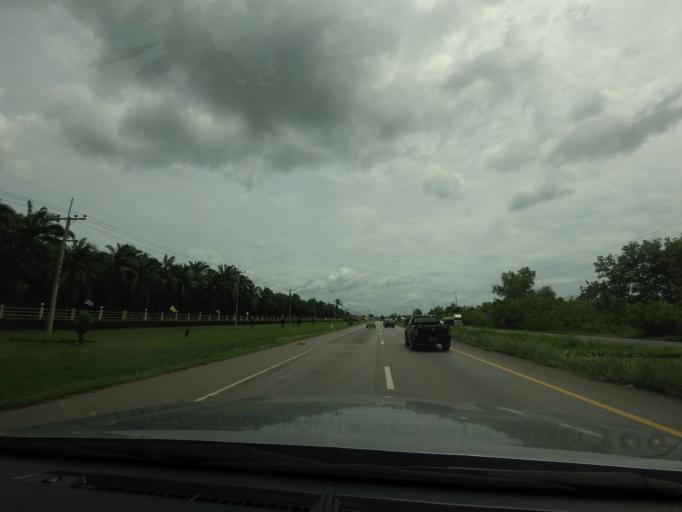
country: TH
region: Surat Thani
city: Tha Chang
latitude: 9.2788
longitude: 99.1496
